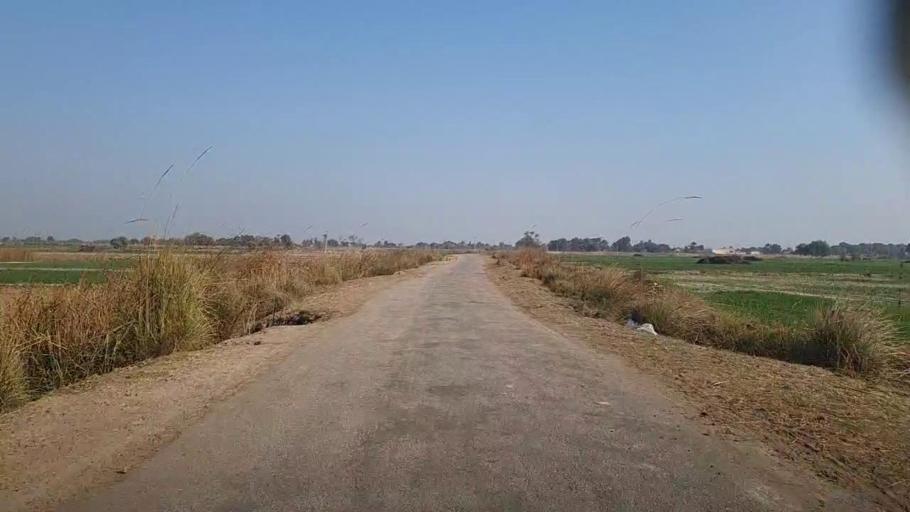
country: PK
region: Sindh
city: Mirpur Mathelo
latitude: 27.8745
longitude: 69.6284
